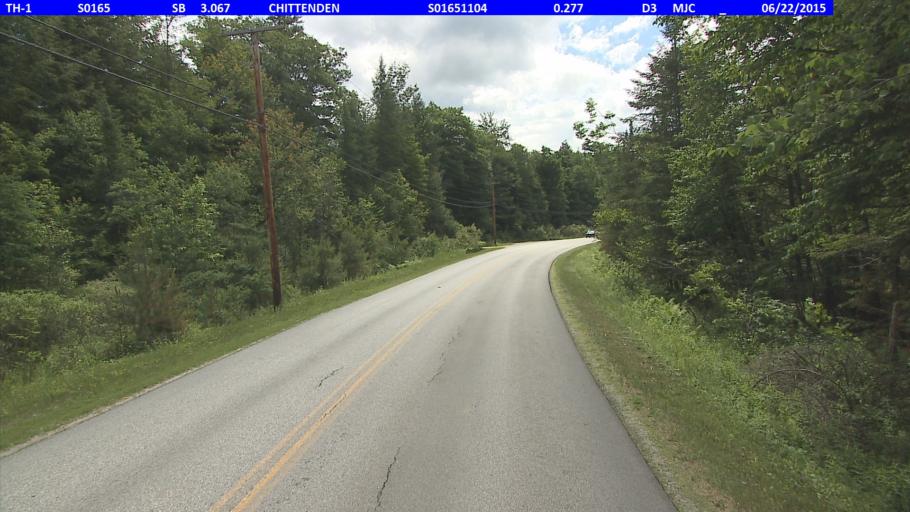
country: US
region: Vermont
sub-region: Rutland County
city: Rutland
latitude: 43.6815
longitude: -72.9468
